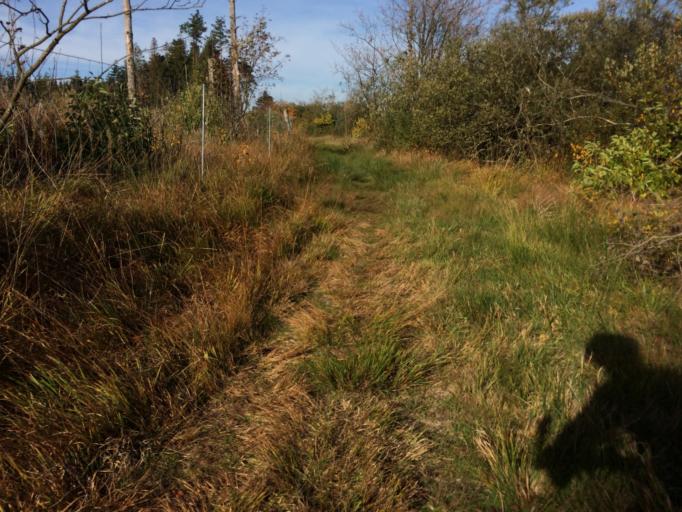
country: DK
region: Central Jutland
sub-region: Holstebro Kommune
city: Ulfborg
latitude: 56.2767
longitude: 8.4706
